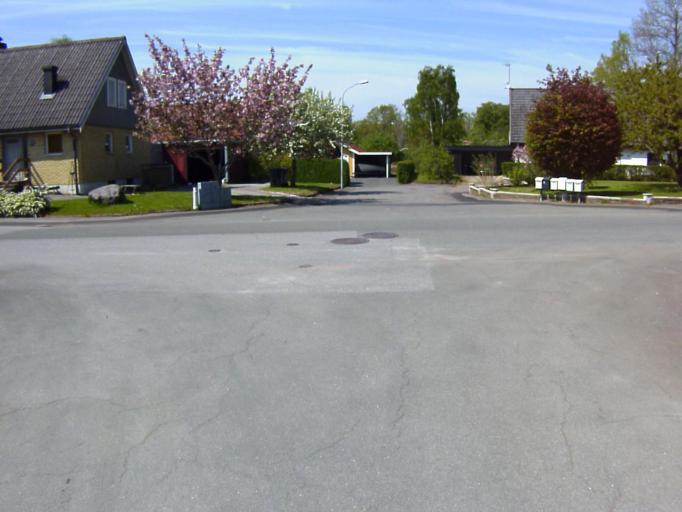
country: SE
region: Skane
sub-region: Kristianstads Kommun
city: Tollarp
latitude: 56.1678
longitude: 14.2910
